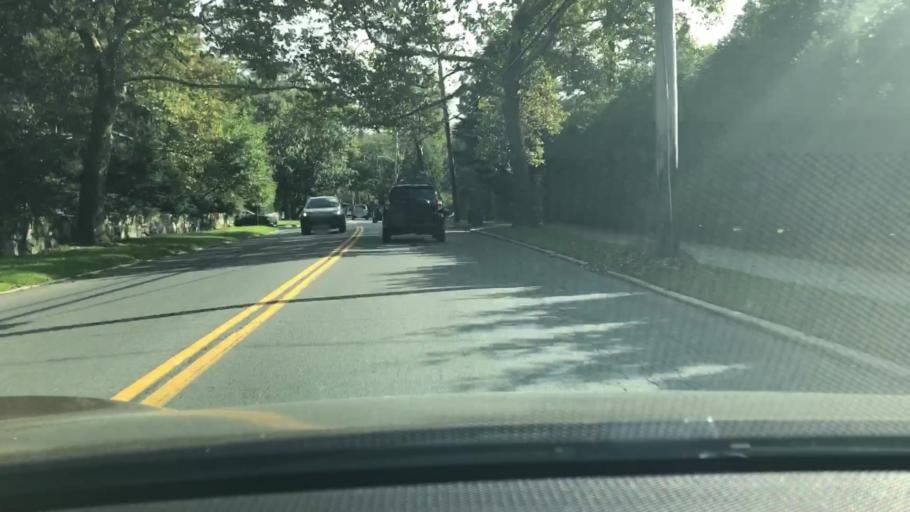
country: US
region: New York
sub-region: Westchester County
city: Bronxville
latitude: 40.9398
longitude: -73.8203
